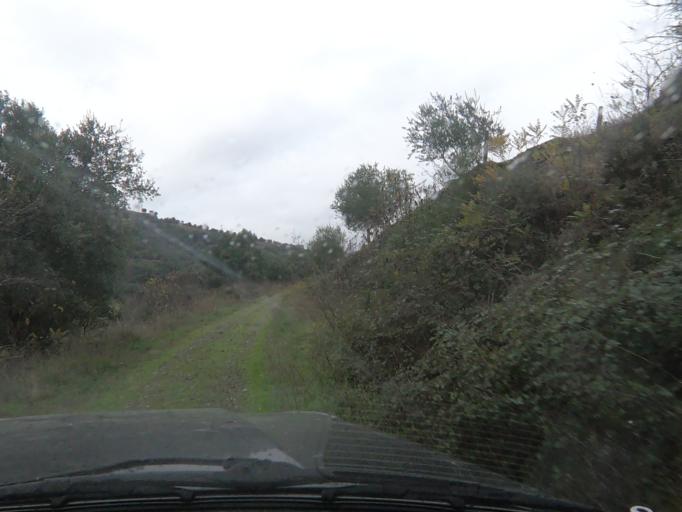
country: PT
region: Vila Real
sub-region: Peso da Regua
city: Peso da Regua
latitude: 41.1827
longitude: -7.7597
